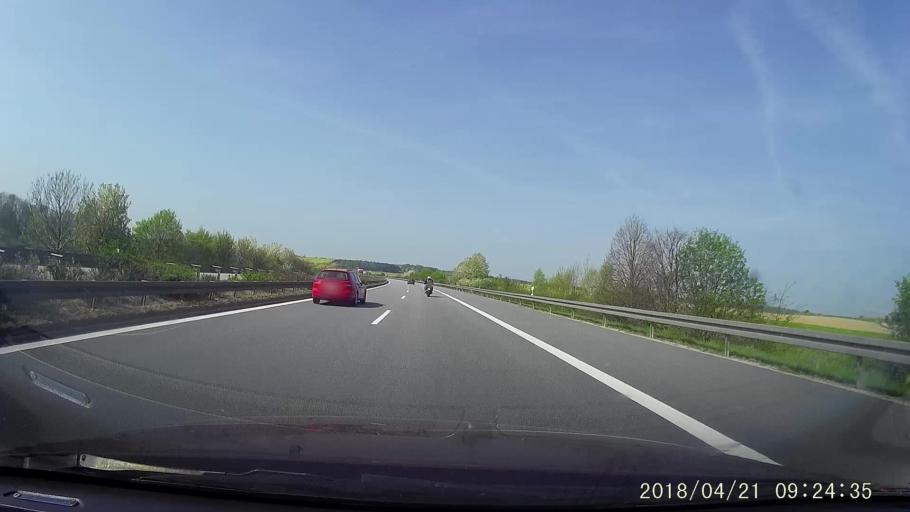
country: DE
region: Saxony
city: Malschwitz
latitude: 51.2076
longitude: 14.4953
